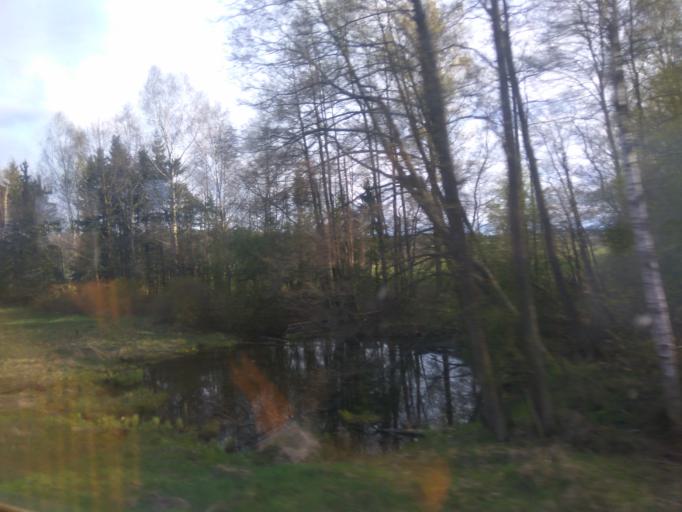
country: LV
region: Babite
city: Pinki
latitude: 56.9647
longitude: 23.9168
